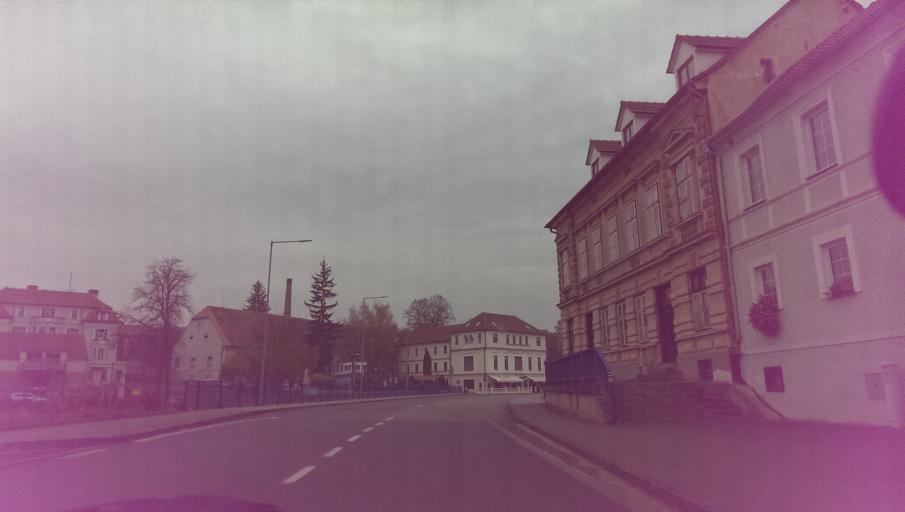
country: AT
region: Lower Austria
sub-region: Politischer Bezirk Hollabrunn
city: Hardegg
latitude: 48.8953
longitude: 15.8119
